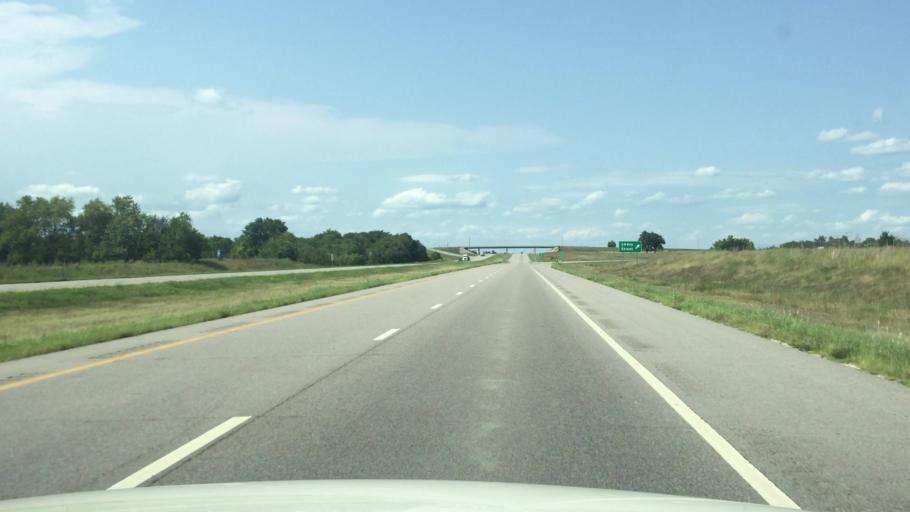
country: US
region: Kansas
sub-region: Linn County
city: La Cygne
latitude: 38.3949
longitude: -94.6875
